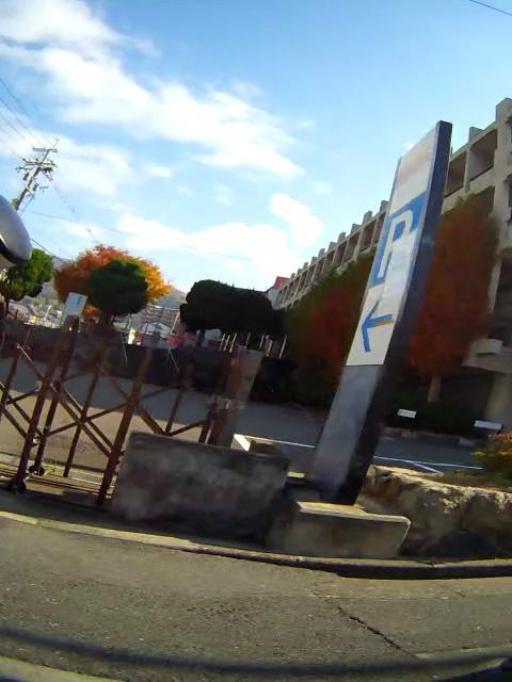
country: JP
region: Osaka
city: Yao
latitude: 34.6585
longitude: 135.6399
